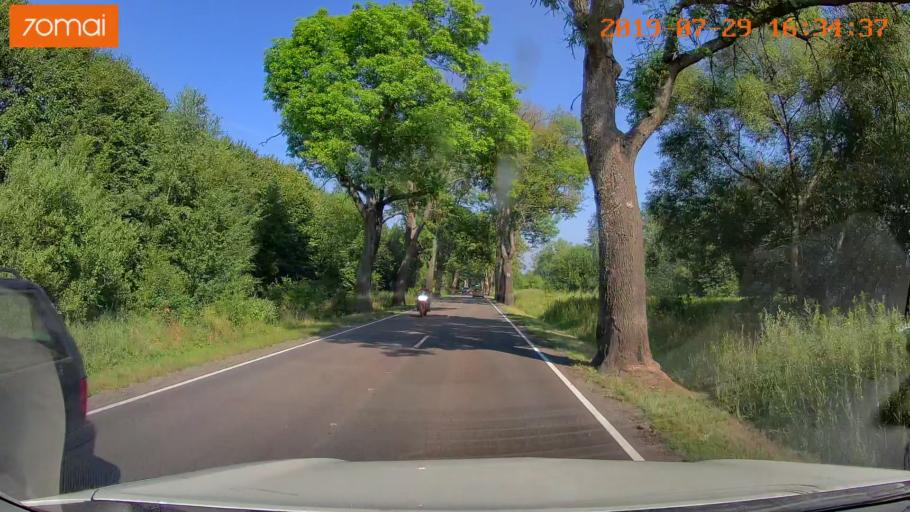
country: RU
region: Kaliningrad
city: Primorsk
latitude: 54.7400
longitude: 20.0557
